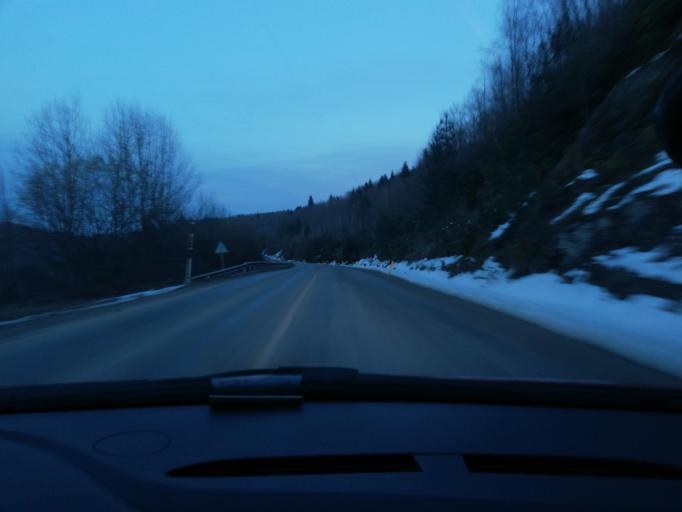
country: TR
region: Kastamonu
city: Inebolu
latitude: 41.8986
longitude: 33.7127
